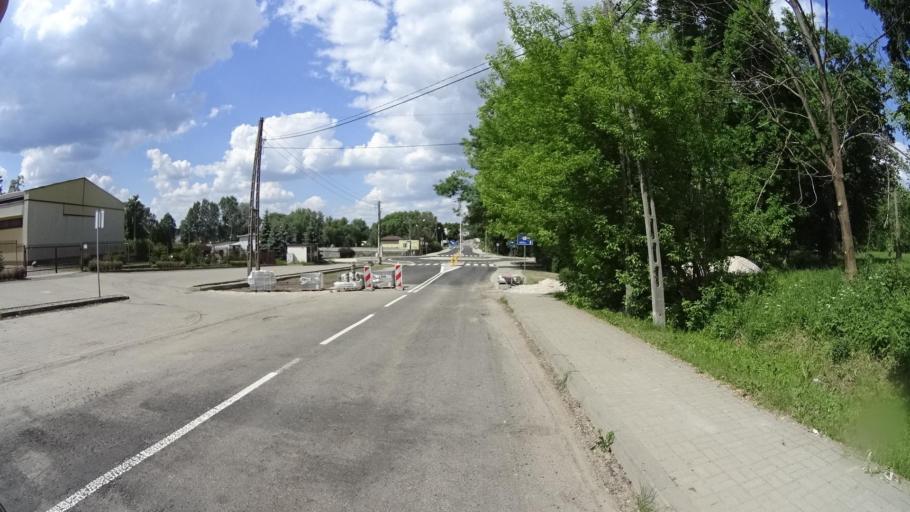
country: PL
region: Masovian Voivodeship
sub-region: Powiat piaseczynski
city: Tarczyn
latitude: 51.9750
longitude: 20.8336
